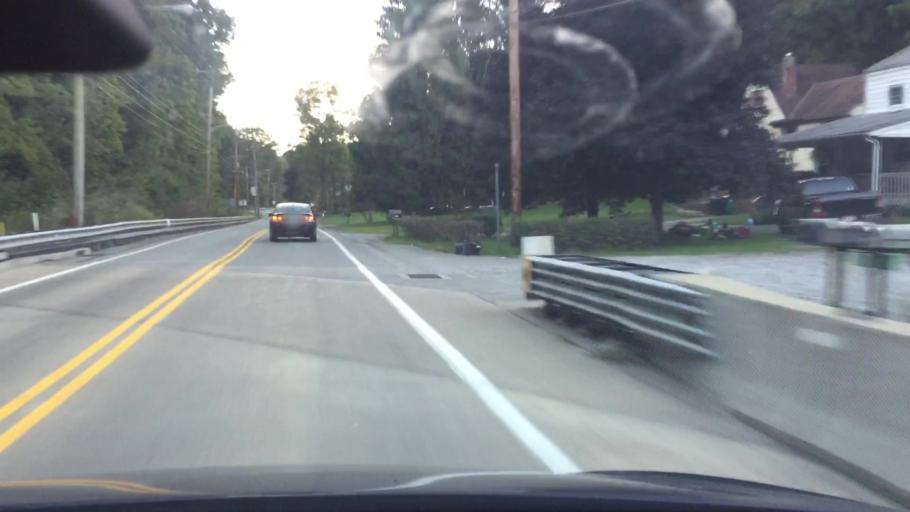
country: US
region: Pennsylvania
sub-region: Allegheny County
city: Allison Park
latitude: 40.5388
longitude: -79.9196
